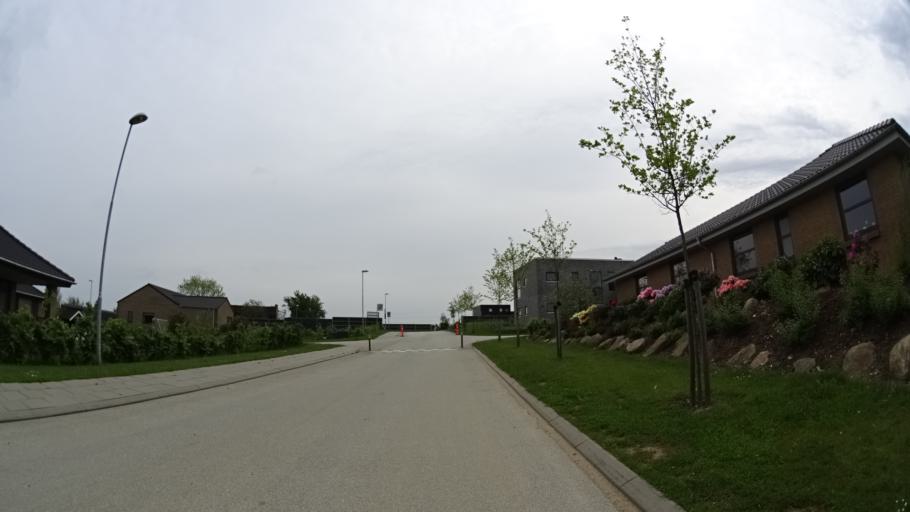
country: DK
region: Central Jutland
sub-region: Arhus Kommune
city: Stavtrup
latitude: 56.1298
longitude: 10.1062
